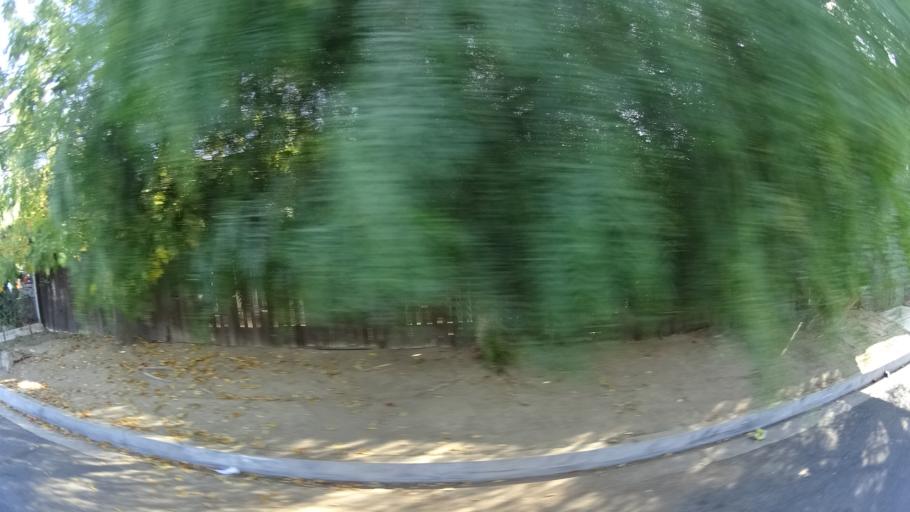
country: US
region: California
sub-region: Kern County
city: Bakersfield
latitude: 35.3963
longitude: -118.9808
